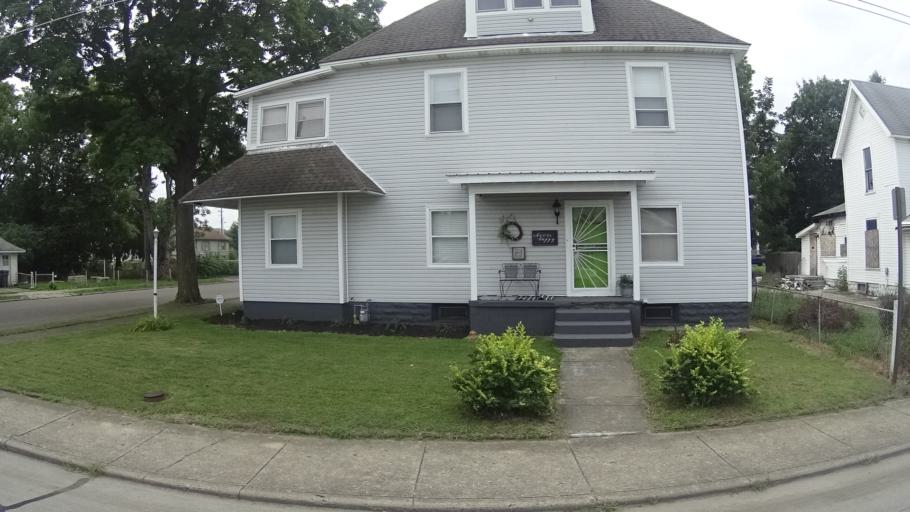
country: US
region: Indiana
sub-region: Madison County
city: Anderson
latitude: 40.1044
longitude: -85.6911
